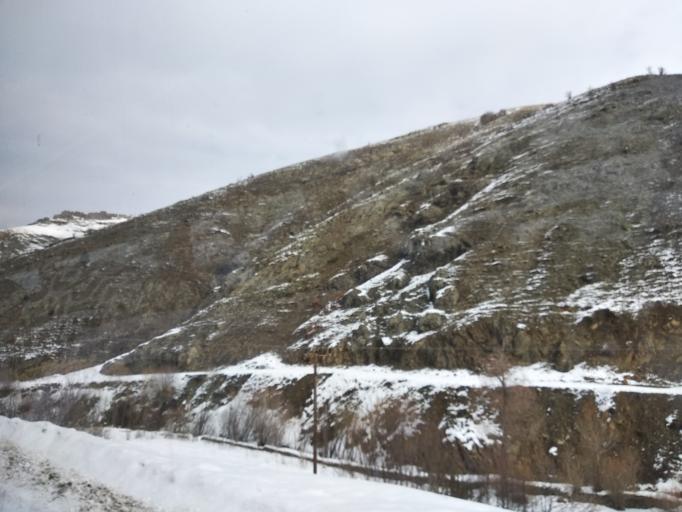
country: TR
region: Gumushane
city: Gumushkhane
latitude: 40.2904
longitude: 39.4829
